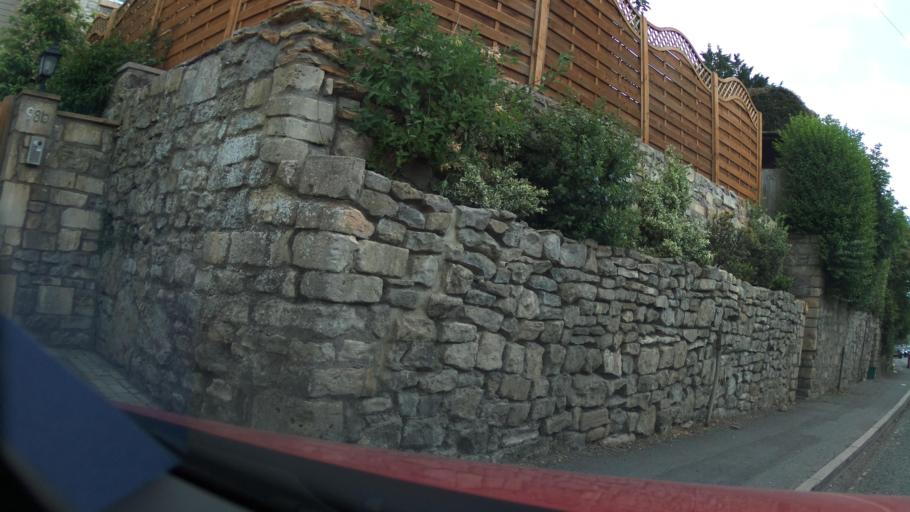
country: GB
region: England
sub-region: Bath and North East Somerset
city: Bath
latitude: 51.3979
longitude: -2.3951
